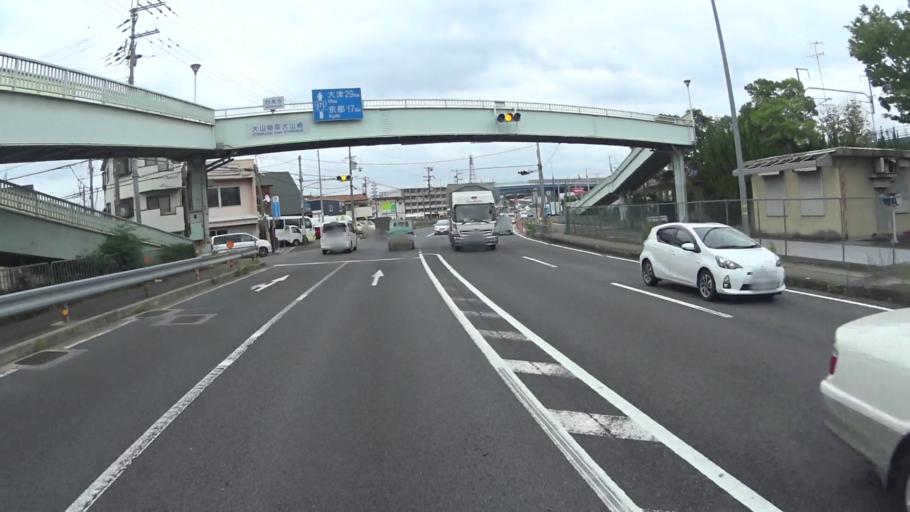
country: JP
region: Kyoto
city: Yawata
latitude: 34.9002
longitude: 135.6900
